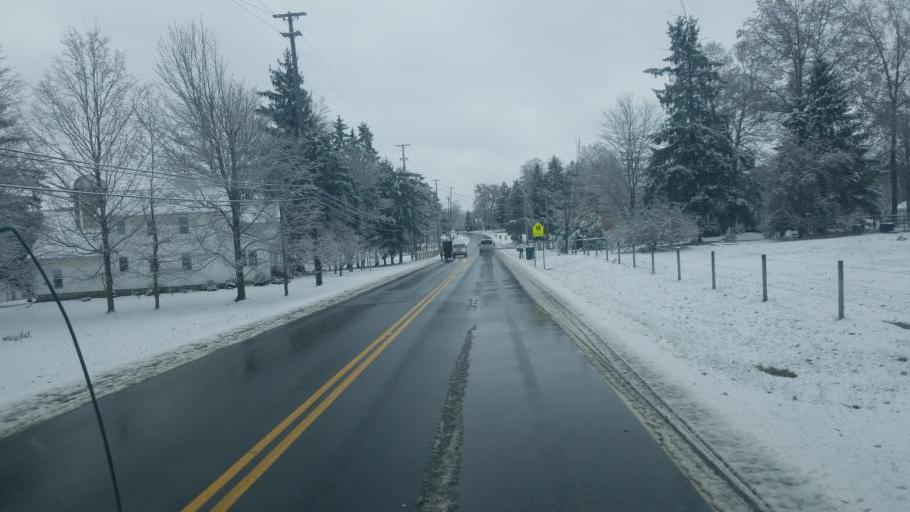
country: US
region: Ohio
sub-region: Geauga County
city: Middlefield
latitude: 41.4503
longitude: -81.1012
